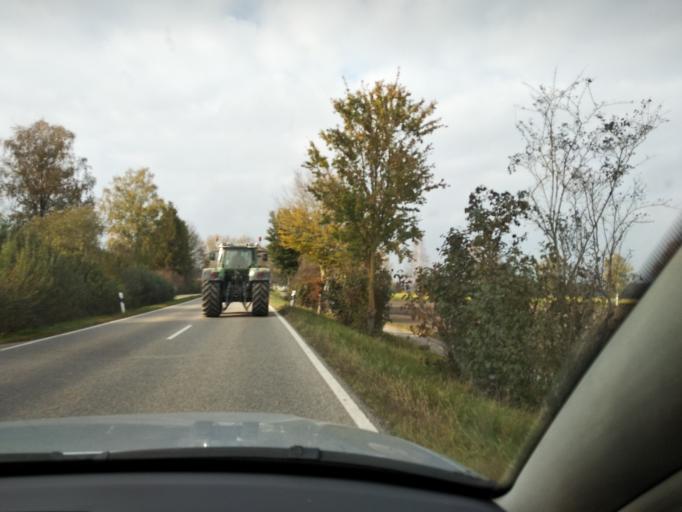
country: DE
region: Bavaria
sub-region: Upper Bavaria
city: Markt Schwaben
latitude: 48.1771
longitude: 11.8840
